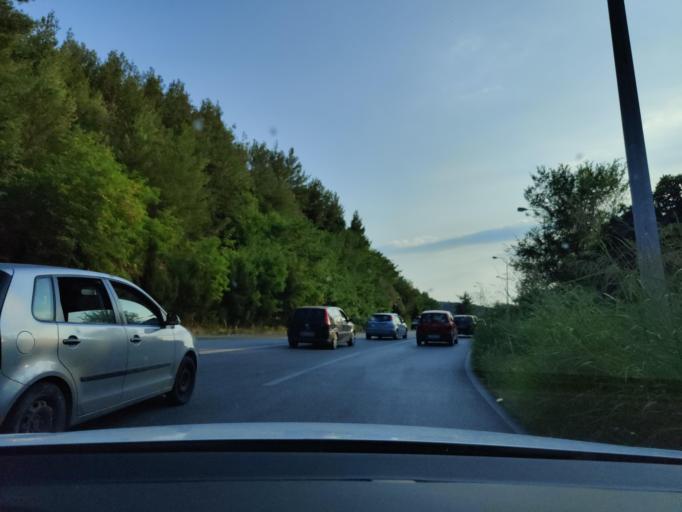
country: GR
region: East Macedonia and Thrace
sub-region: Nomos Kavalas
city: Amygdaleonas
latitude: 40.9505
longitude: 24.3718
